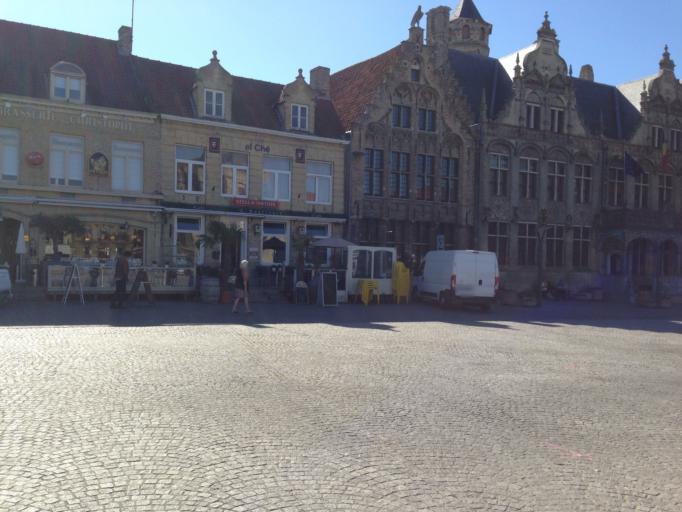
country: BE
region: Flanders
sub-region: Provincie West-Vlaanderen
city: Veurne
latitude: 51.0724
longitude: 2.6621
